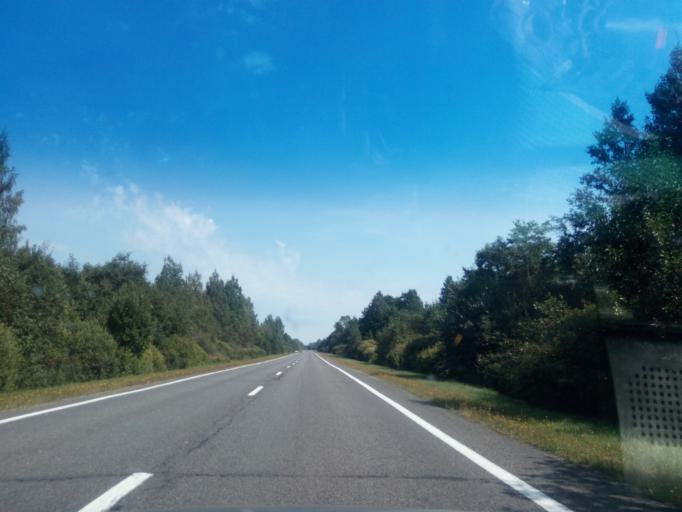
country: BY
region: Vitebsk
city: Vyerkhnyadzvinsk
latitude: 55.8252
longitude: 27.7924
